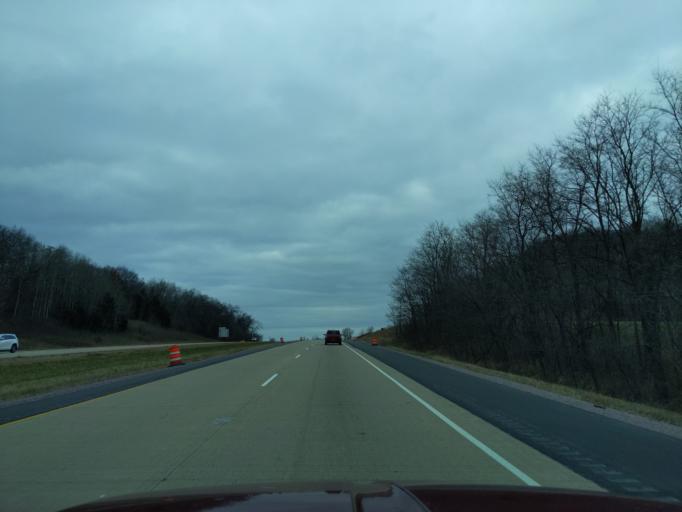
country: US
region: Wisconsin
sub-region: Columbia County
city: Portage
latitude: 43.5960
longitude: -89.4687
